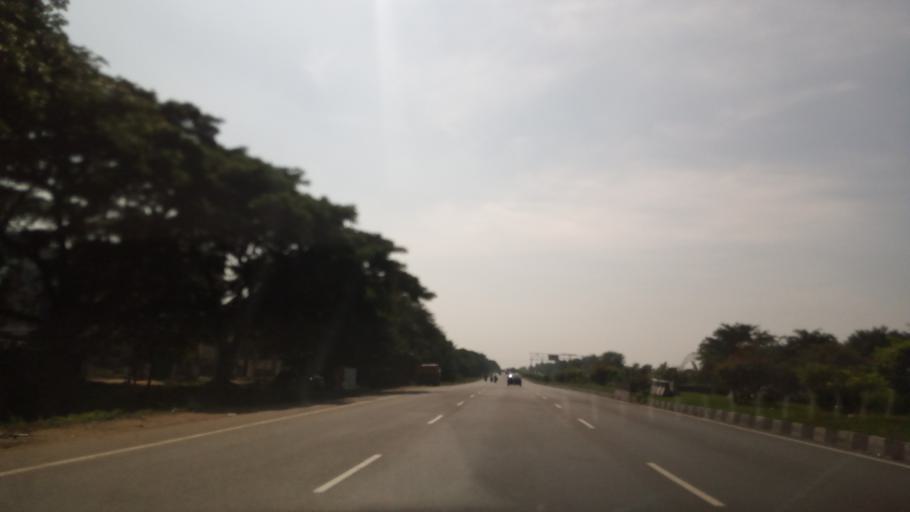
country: IN
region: Tamil Nadu
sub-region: Vellore
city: Ambur
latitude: 12.7375
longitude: 78.6884
